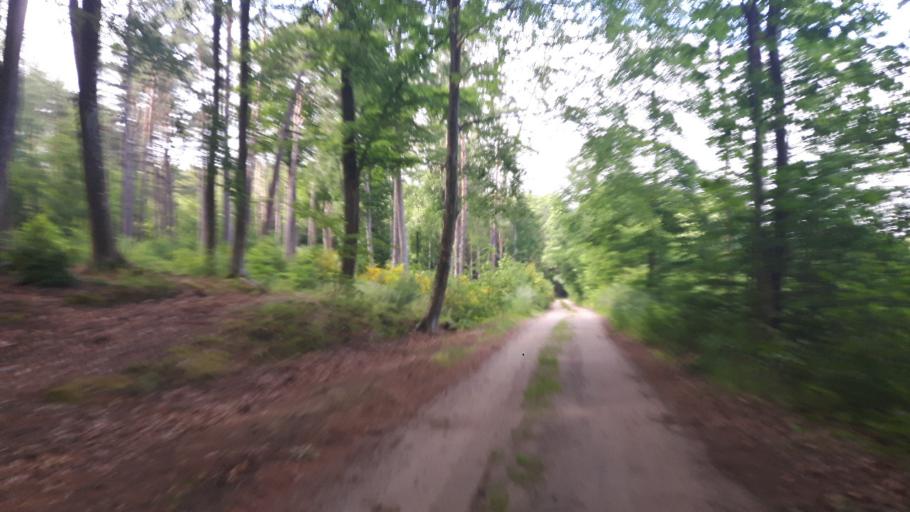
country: PL
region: Pomeranian Voivodeship
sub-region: Slupsk
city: Slupsk
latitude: 54.6068
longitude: 17.0214
